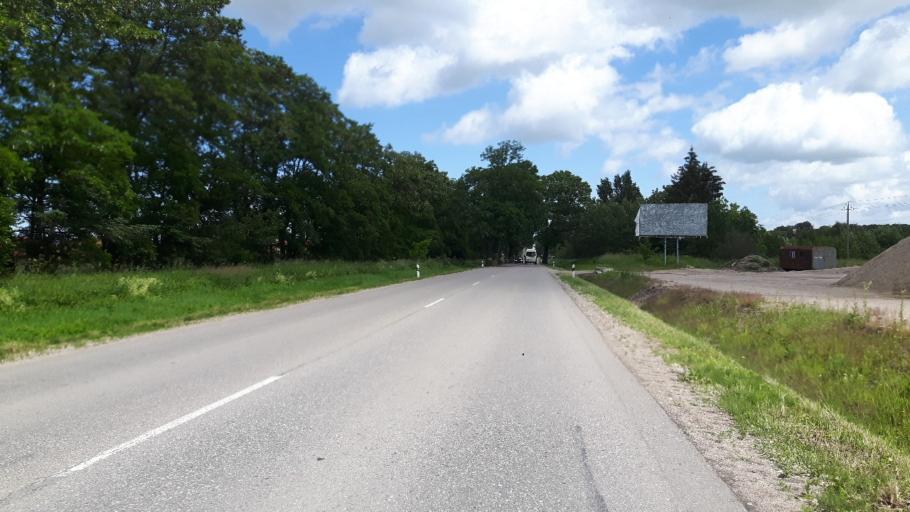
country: RU
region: Kaliningrad
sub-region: Zelenogradskiy Rayon
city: Zelenogradsk
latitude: 54.9361
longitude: 20.4433
